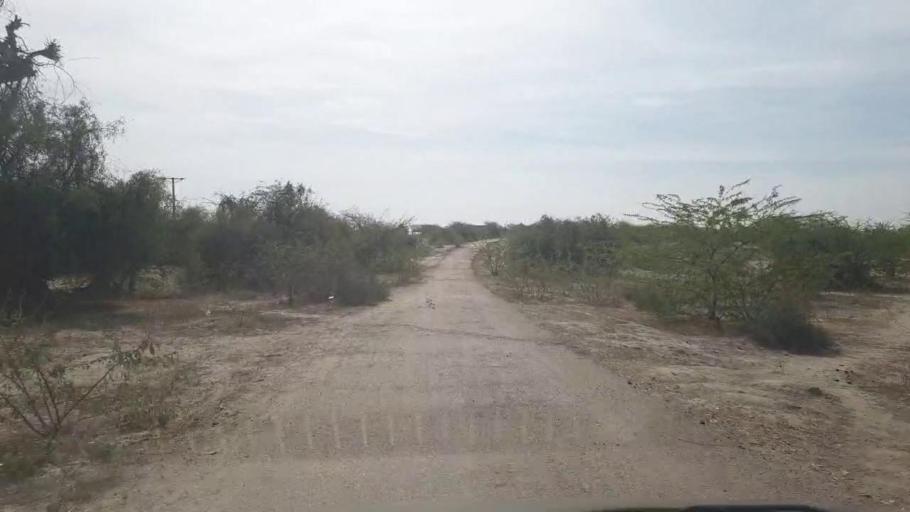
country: PK
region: Sindh
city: Umarkot
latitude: 25.2959
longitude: 69.7446
